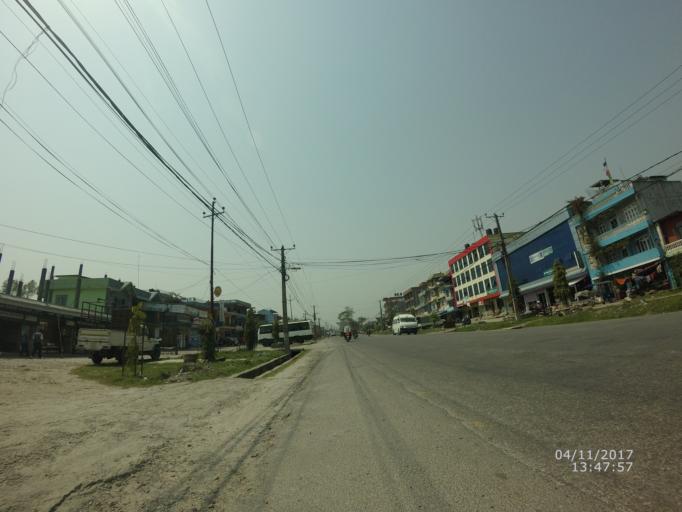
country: NP
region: Western Region
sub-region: Gandaki Zone
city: Pokhara
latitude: 28.1835
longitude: 84.0377
